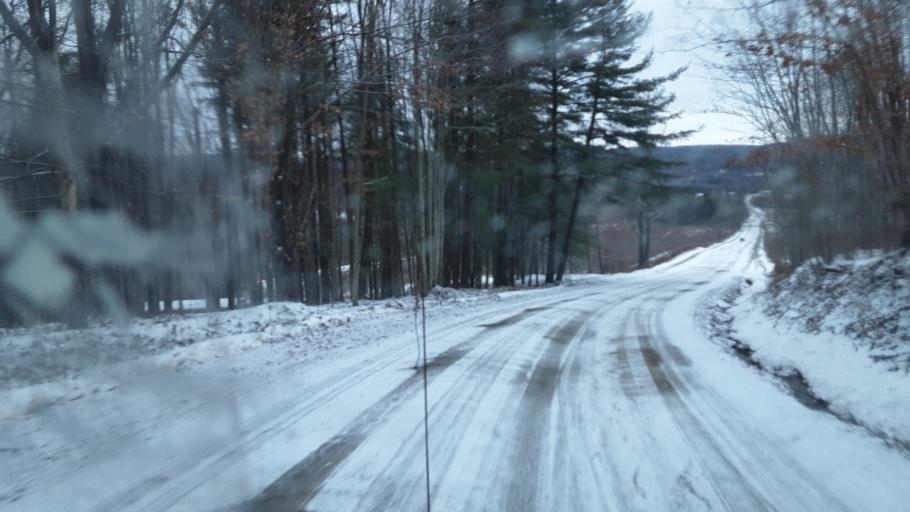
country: US
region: New York
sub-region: Allegany County
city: Friendship
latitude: 42.2865
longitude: -78.1622
